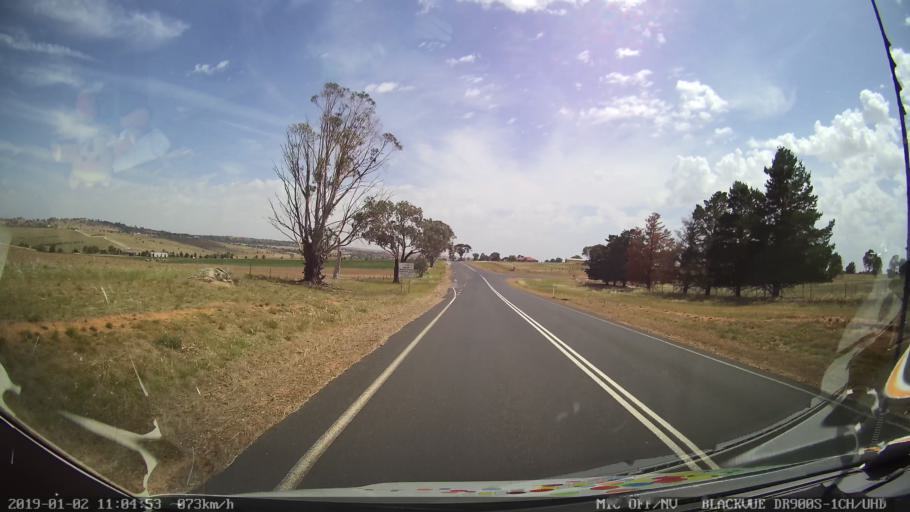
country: AU
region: New South Wales
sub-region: Young
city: Young
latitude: -34.5714
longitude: 148.3539
